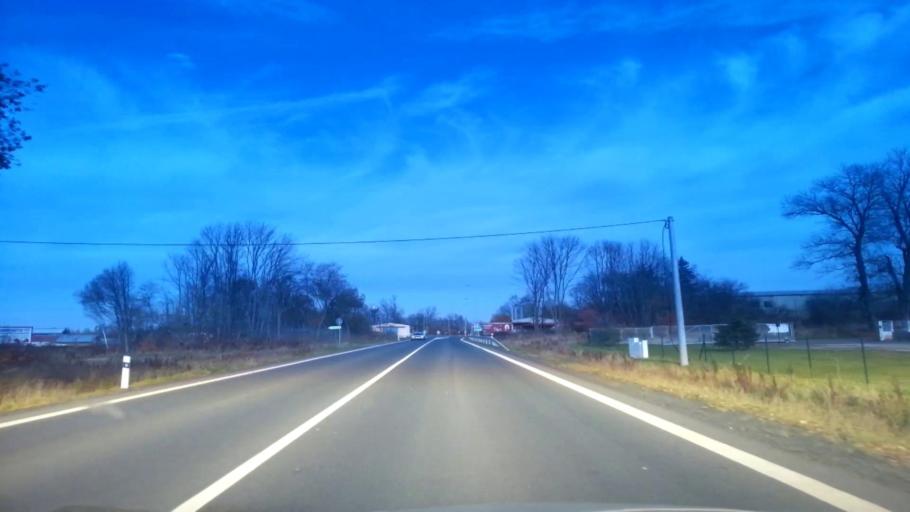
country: CZ
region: Karlovarsky
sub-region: Okres Cheb
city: Cheb
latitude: 50.0633
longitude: 12.3834
